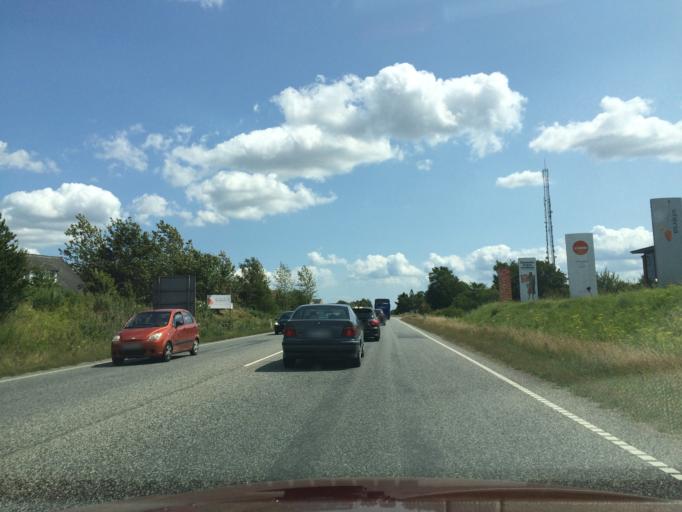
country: DK
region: Central Jutland
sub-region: Favrskov Kommune
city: Soften
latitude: 56.1861
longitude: 10.0924
